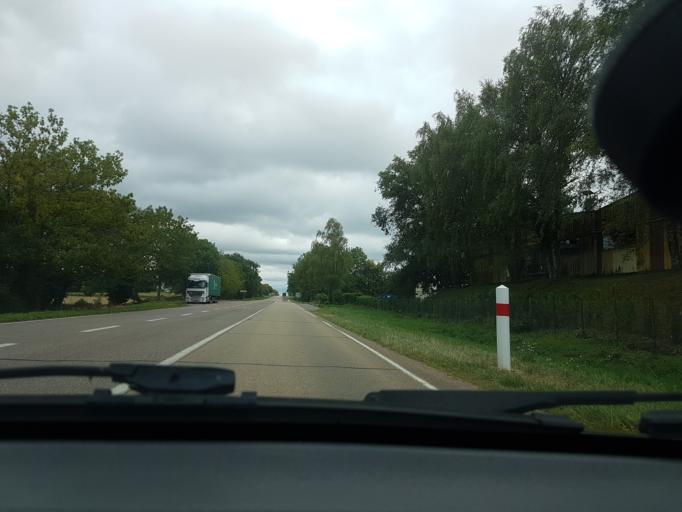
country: FR
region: Bourgogne
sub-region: Departement de la Cote-d'Or
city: Saulieu
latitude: 47.4276
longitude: 4.1067
